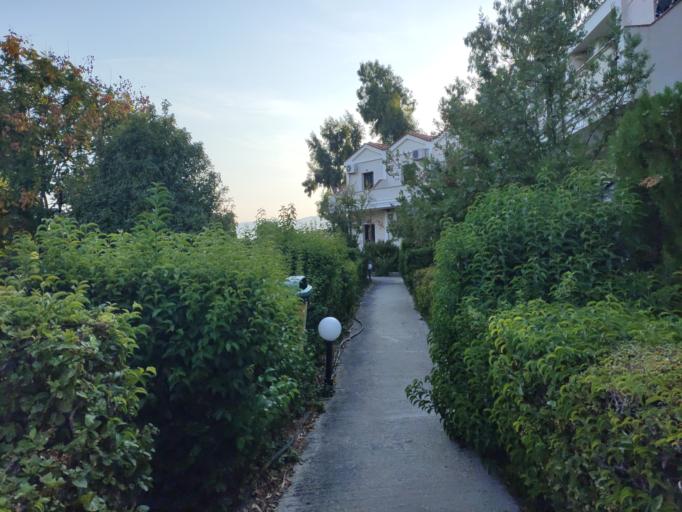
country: GR
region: North Aegean
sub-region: Nomos Lesvou
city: Kalloni
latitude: 39.2096
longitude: 26.2056
